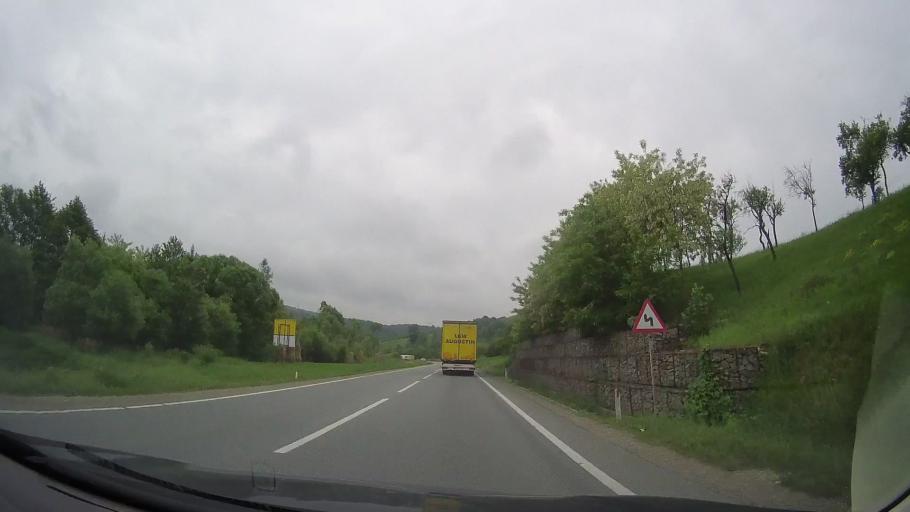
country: RO
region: Caras-Severin
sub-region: Comuna Teregova
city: Teregova
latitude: 45.1447
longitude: 22.3081
